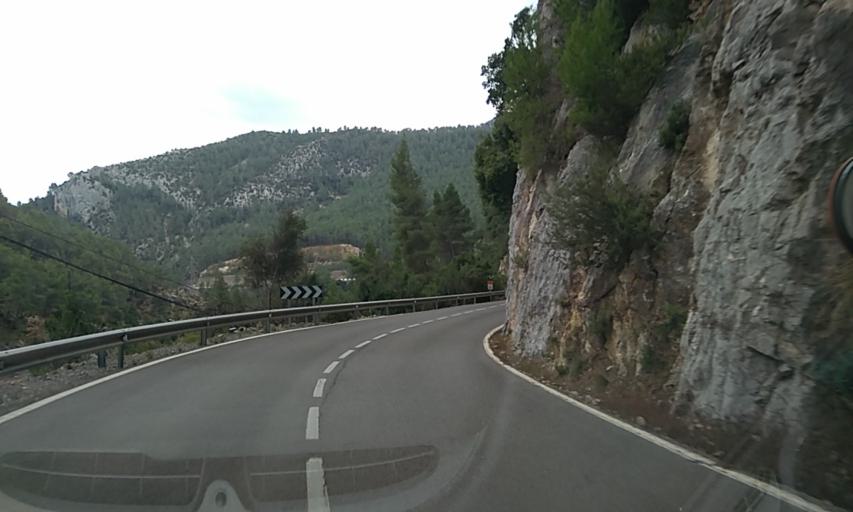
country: ES
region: Valencia
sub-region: Provincia de Castello
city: Montanejos
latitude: 40.0793
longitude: -0.5391
